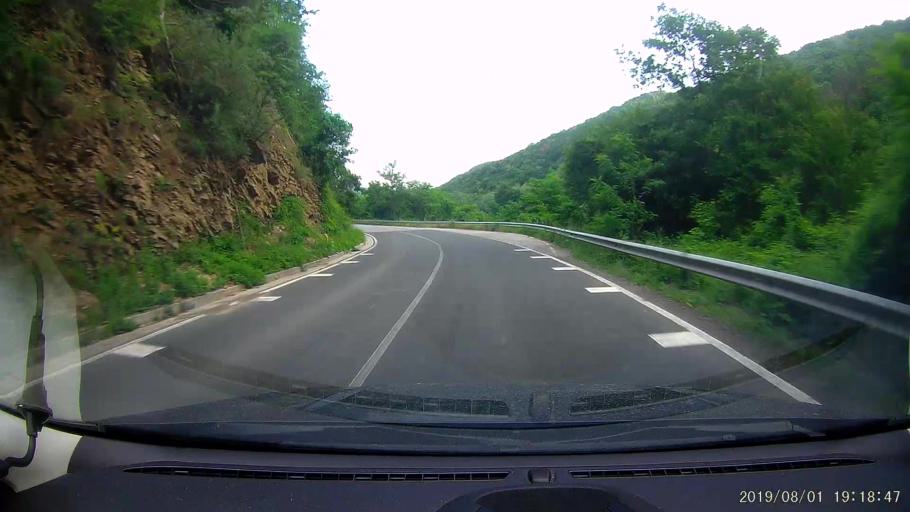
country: BG
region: Shumen
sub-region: Obshtina Smyadovo
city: Smyadovo
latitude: 42.9081
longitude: 26.9402
